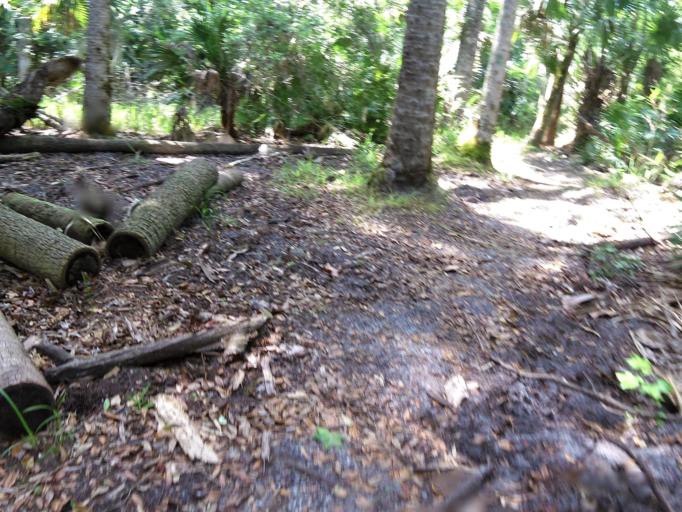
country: US
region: Florida
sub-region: Flagler County
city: Flagler Beach
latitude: 29.4176
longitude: -81.1350
